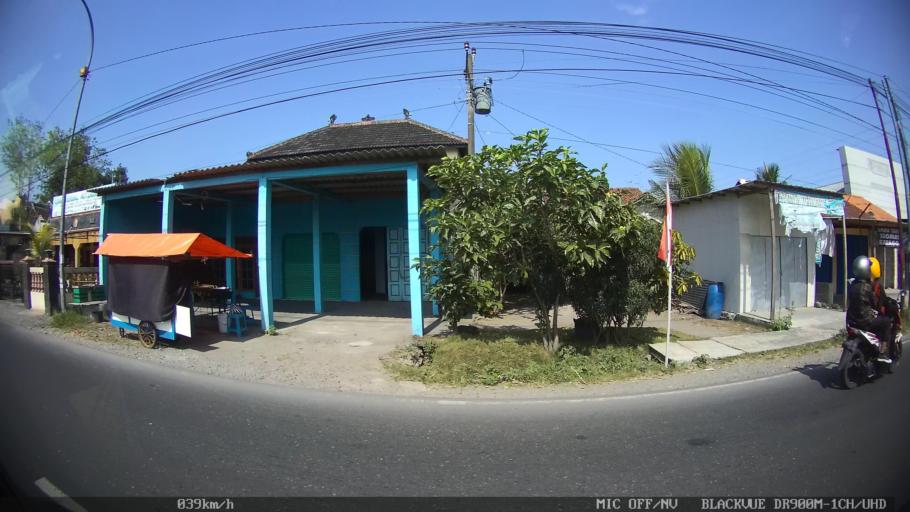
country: ID
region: Daerah Istimewa Yogyakarta
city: Sewon
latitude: -7.8826
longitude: 110.3891
